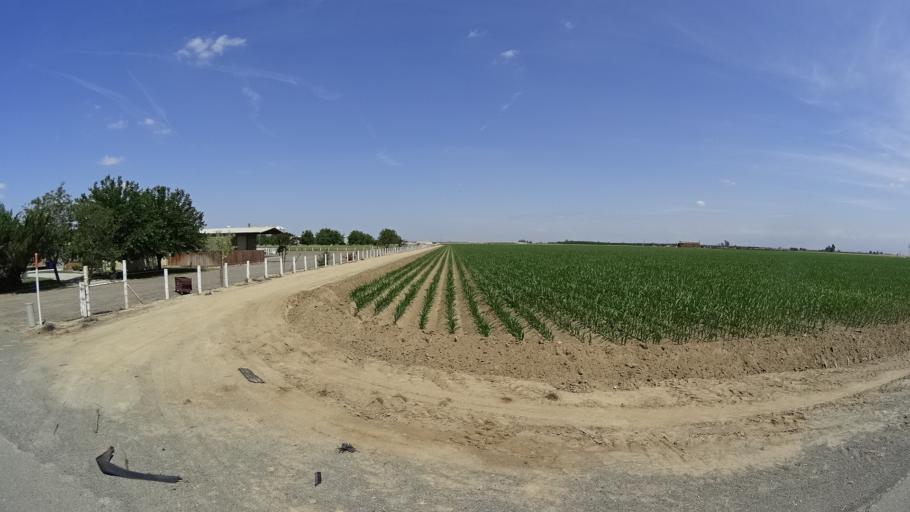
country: US
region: California
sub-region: Tulare County
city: Goshen
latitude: 36.2978
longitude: -119.4873
